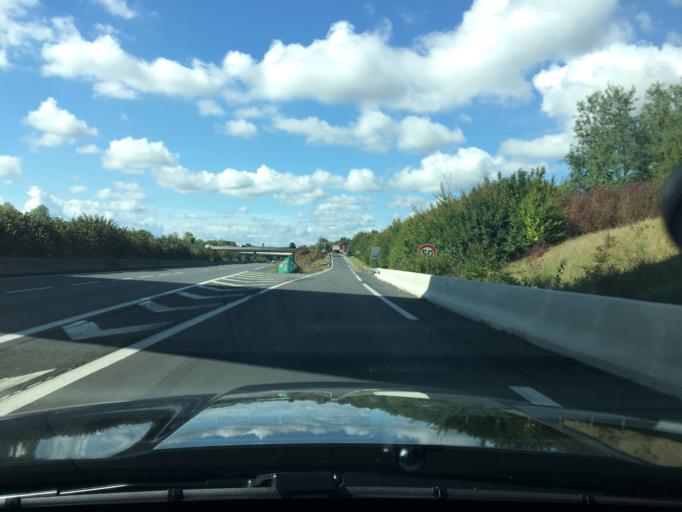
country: FR
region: Ile-de-France
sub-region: Departement du Val-d'Oise
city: Louvres
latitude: 49.0284
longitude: 2.5048
